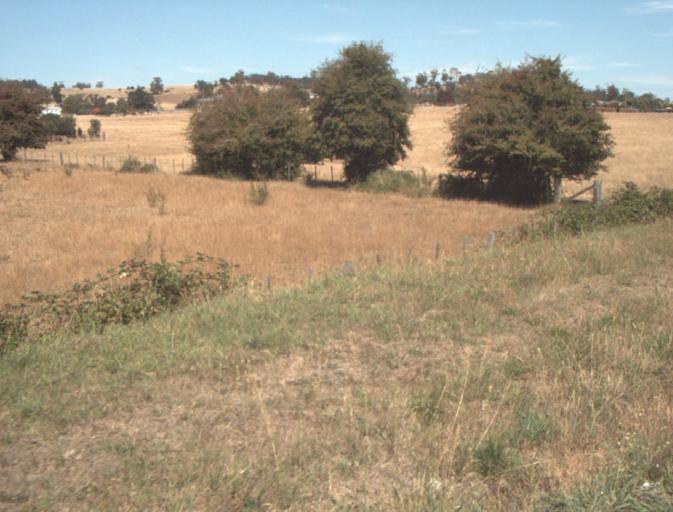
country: AU
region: Tasmania
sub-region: Launceston
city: Mayfield
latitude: -41.3676
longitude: 147.1414
